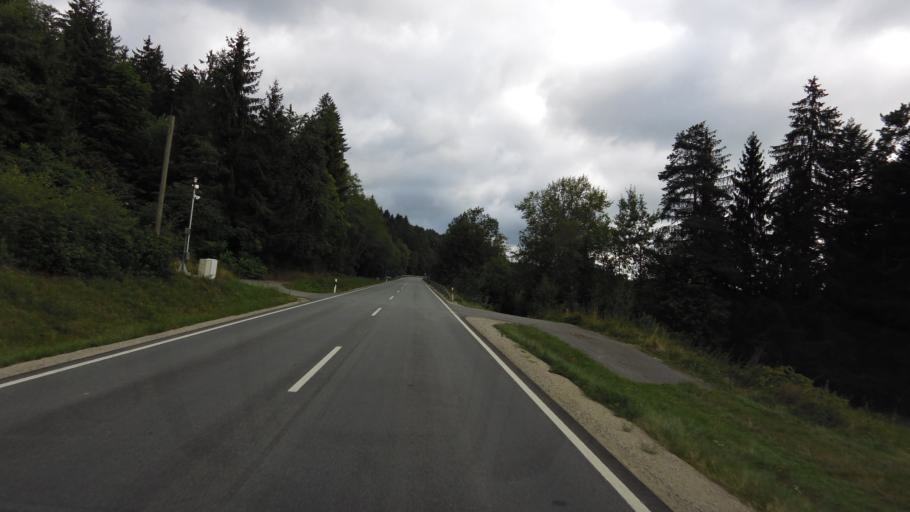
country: DE
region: Bavaria
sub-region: Lower Bavaria
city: Loitzendorf
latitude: 49.0982
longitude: 12.6471
